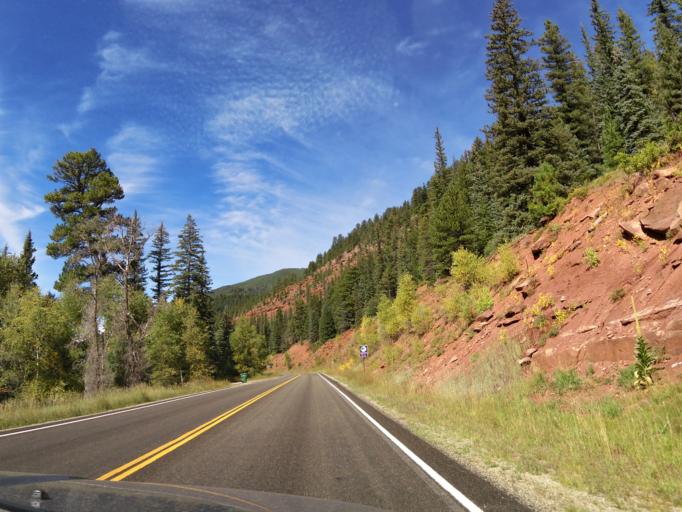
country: US
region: Colorado
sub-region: Montezuma County
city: Mancos
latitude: 37.5879
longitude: -108.1523
